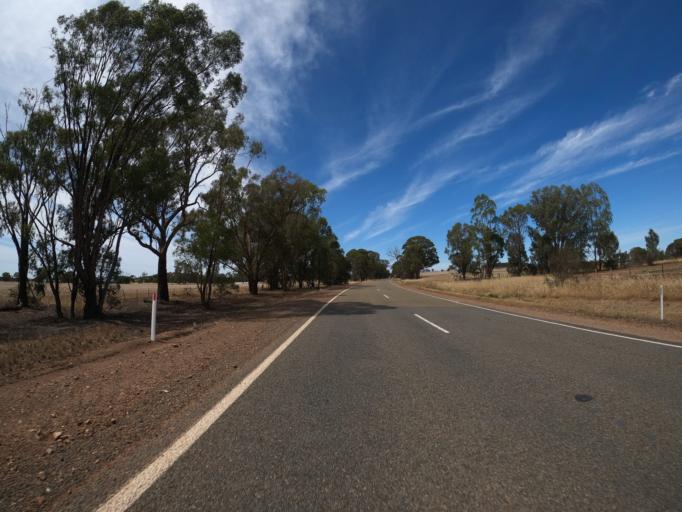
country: AU
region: Victoria
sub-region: Benalla
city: Benalla
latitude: -36.3076
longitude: 145.9583
